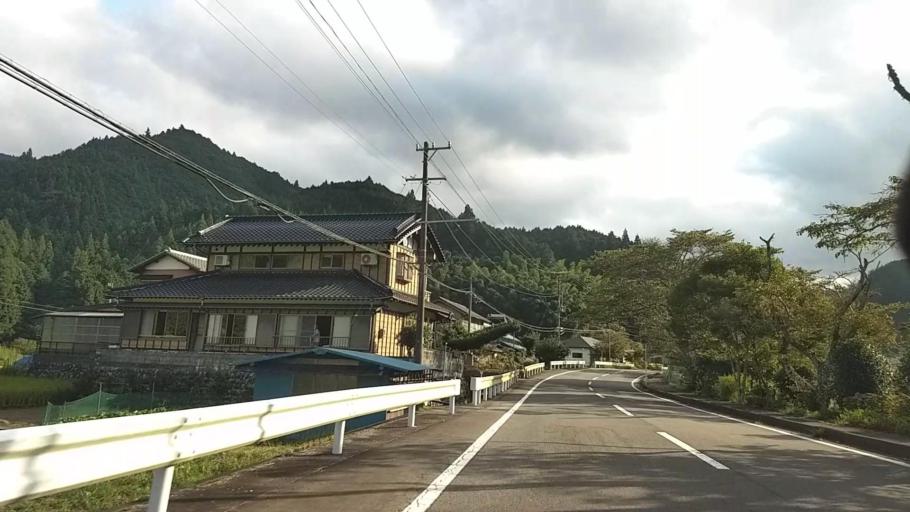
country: JP
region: Shizuoka
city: Fujinomiya
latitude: 35.1793
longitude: 138.5432
